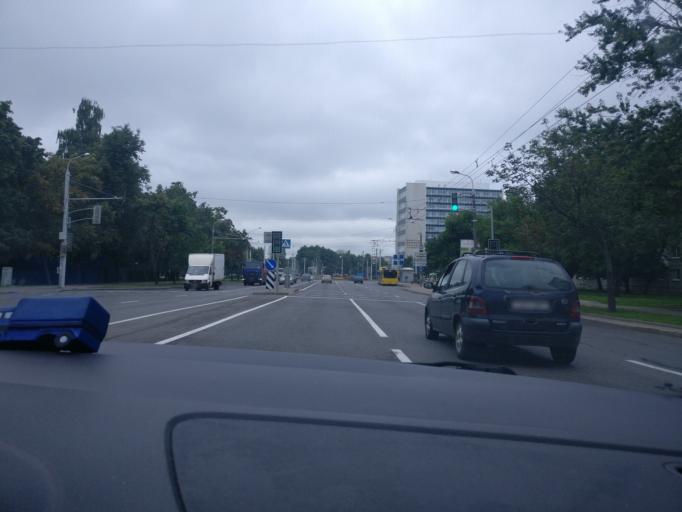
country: BY
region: Minsk
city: Minsk
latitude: 53.8803
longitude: 27.6108
